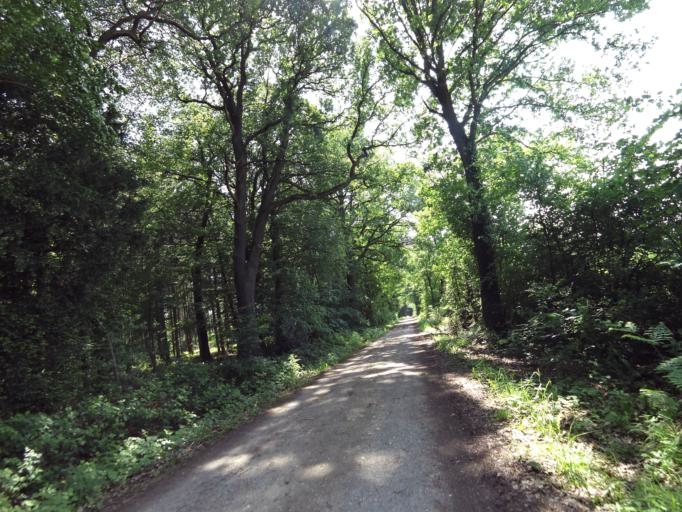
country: DE
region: North Rhine-Westphalia
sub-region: Regierungsbezirk Koln
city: Wachtberg
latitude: 50.6782
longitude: 7.1087
